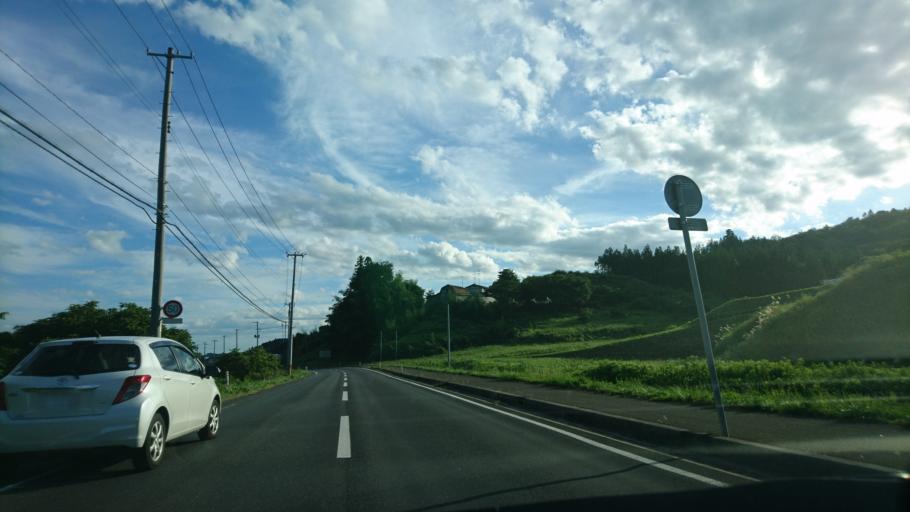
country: JP
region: Iwate
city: Ichinoseki
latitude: 38.8649
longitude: 141.1867
